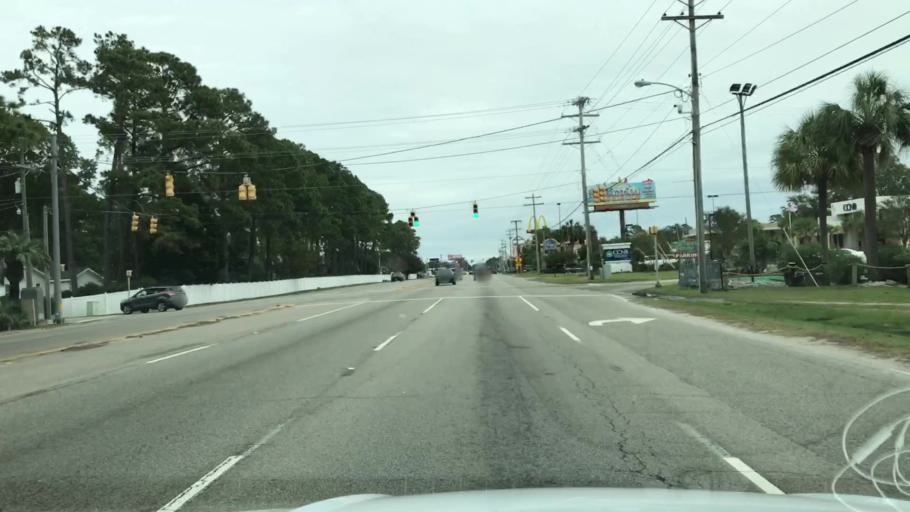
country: US
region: South Carolina
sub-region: Horry County
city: Garden City
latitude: 33.5837
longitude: -79.0153
